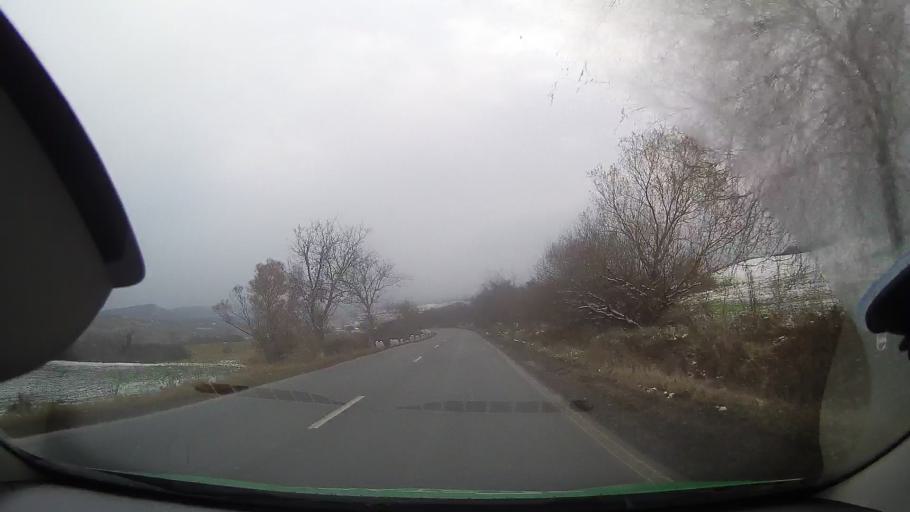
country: RO
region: Sibiu
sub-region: Comuna Blajel
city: Blajel
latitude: 46.2467
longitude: 24.3002
